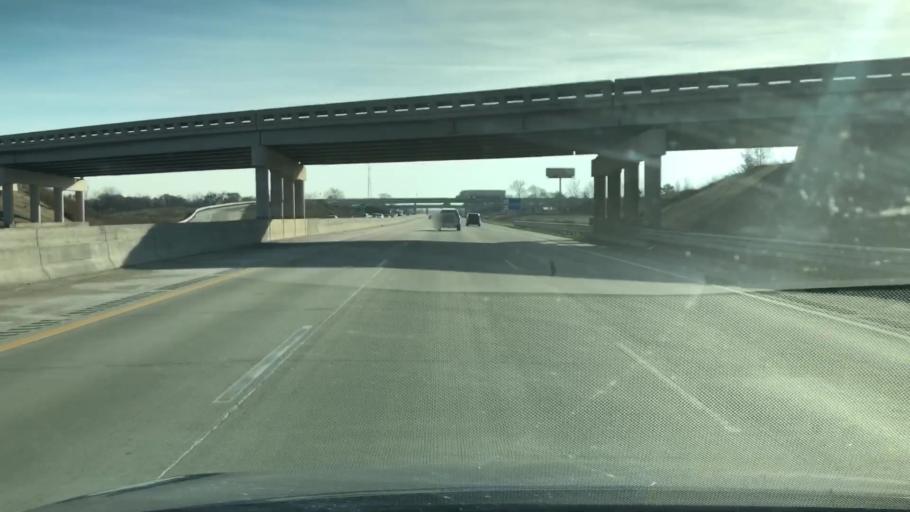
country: US
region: Michigan
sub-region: Saginaw County
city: Buena Vista
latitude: 43.4346
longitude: -83.8939
